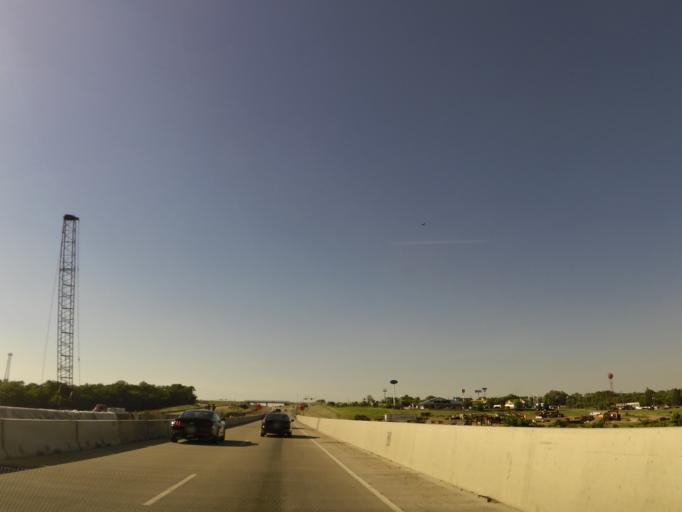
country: US
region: Wisconsin
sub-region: Rock County
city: Edgerton
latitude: 42.8292
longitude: -89.0259
